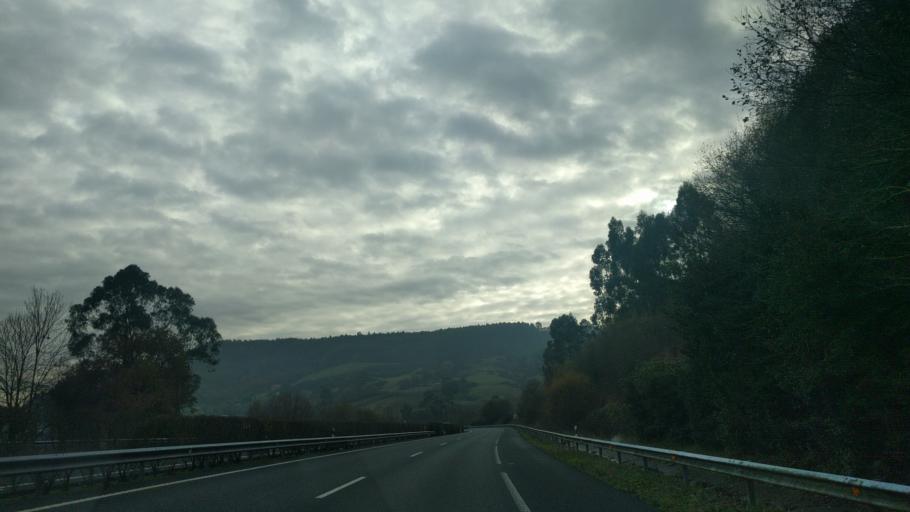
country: ES
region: Cantabria
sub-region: Provincia de Cantabria
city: Barcena de Cicero
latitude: 43.4105
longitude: -3.5171
